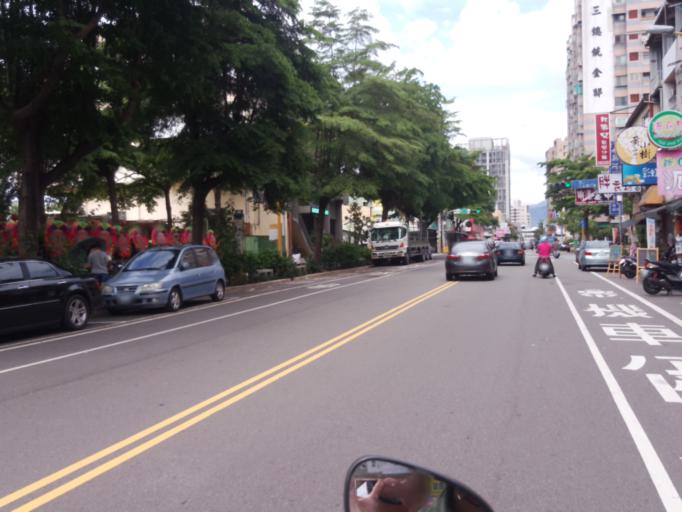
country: TW
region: Taiwan
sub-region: Taichung City
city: Taichung
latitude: 24.1103
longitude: 120.6870
